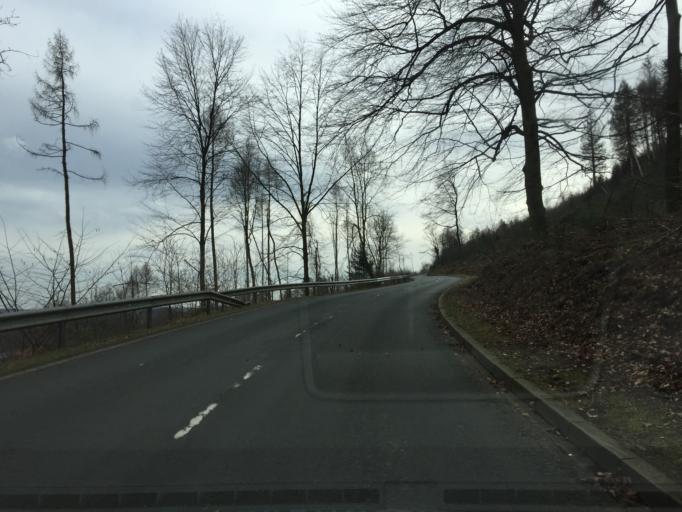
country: DE
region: North Rhine-Westphalia
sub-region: Regierungsbezirk Detmold
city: Detmold
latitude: 51.9185
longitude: 8.8435
